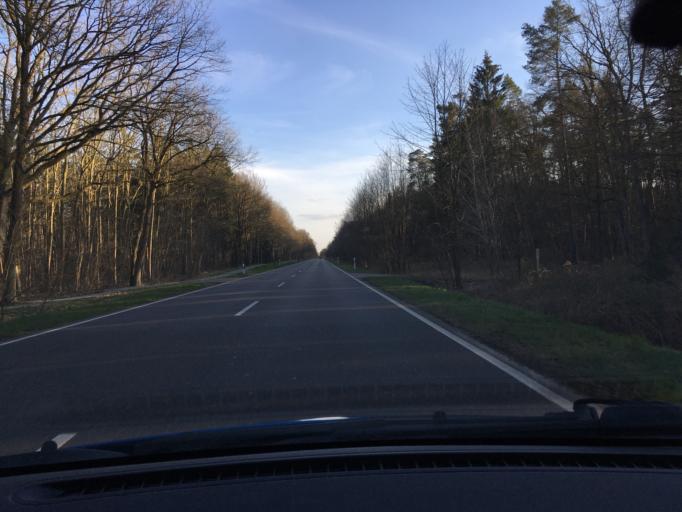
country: DE
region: Mecklenburg-Vorpommern
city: Feldstadt
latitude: 53.5692
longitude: 11.4375
